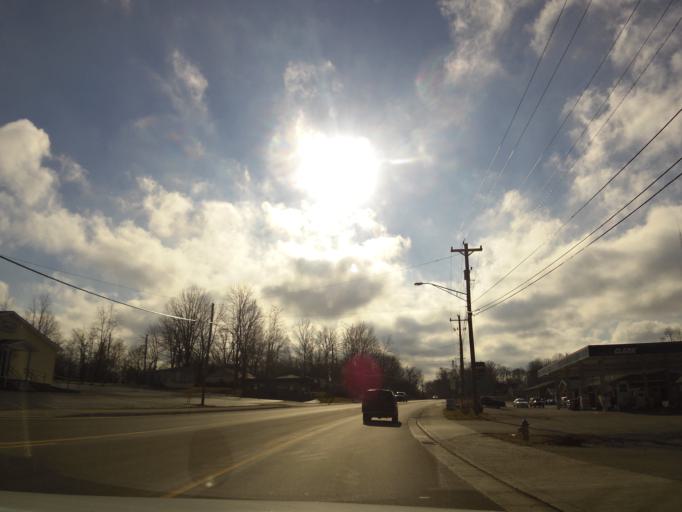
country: US
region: Indiana
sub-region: Jennings County
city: North Vernon
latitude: 38.9953
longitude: -85.6174
